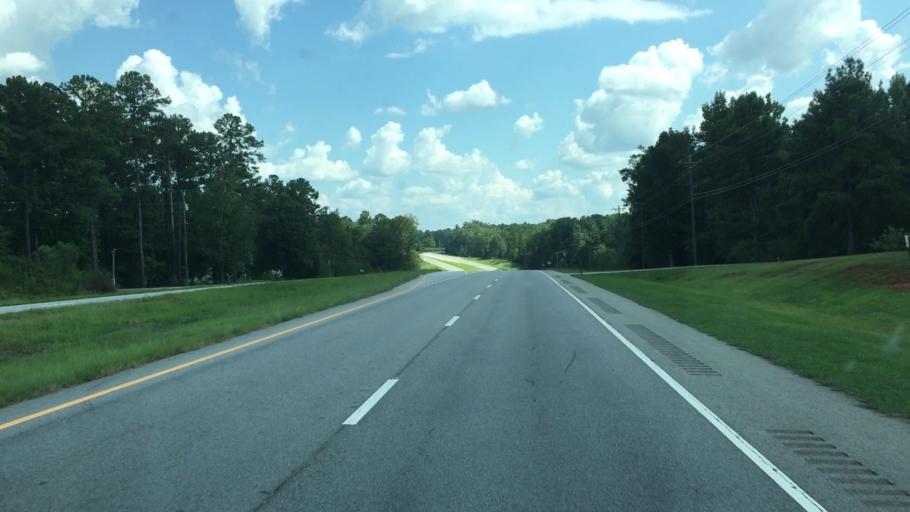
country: US
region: Georgia
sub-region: Putnam County
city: Eatonton
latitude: 33.2450
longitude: -83.3243
